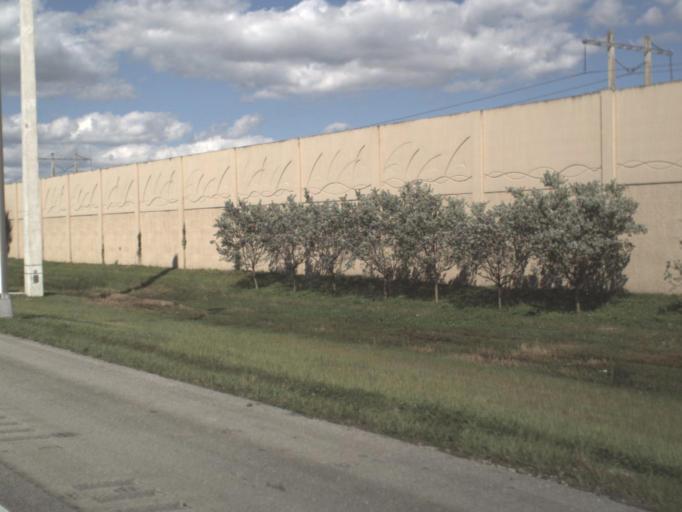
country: US
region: Florida
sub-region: Broward County
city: Broadview Park
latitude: 26.1128
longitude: -80.2183
